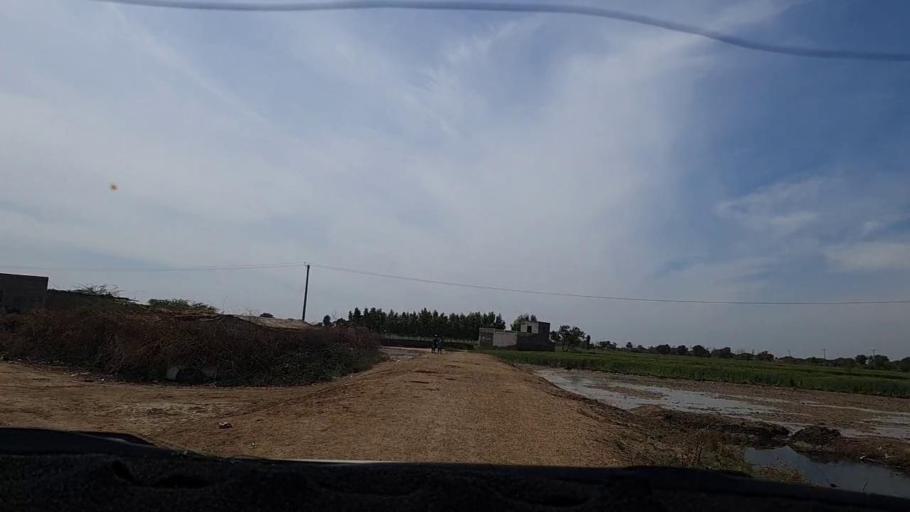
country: PK
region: Sindh
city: Dhoro Naro
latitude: 25.5148
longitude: 69.4778
